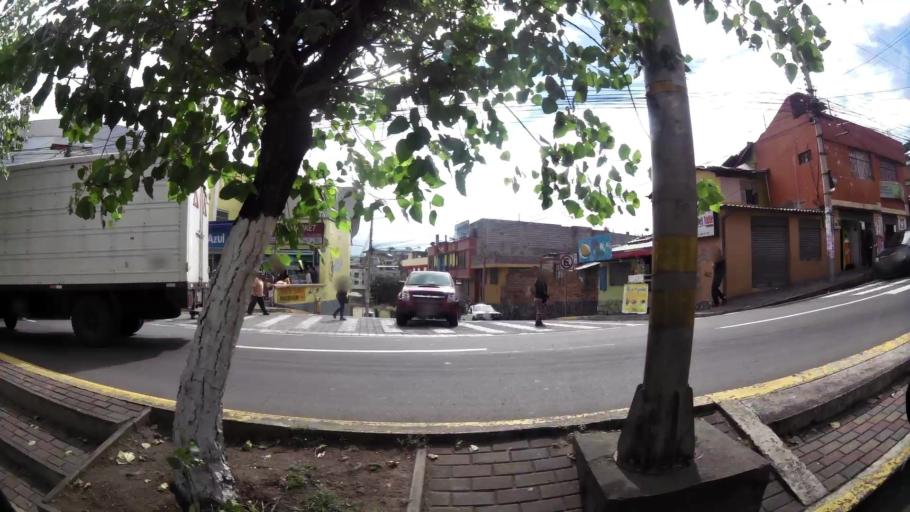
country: EC
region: Pichincha
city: Sangolqui
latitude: -0.3293
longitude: -78.4508
